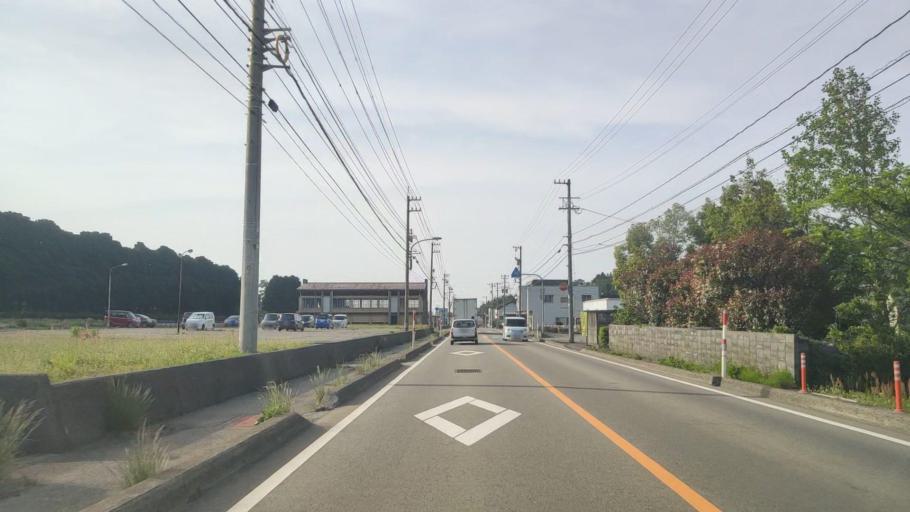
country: JP
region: Toyama
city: Yatsuomachi-higashikumisaka
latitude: 36.5701
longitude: 137.2101
